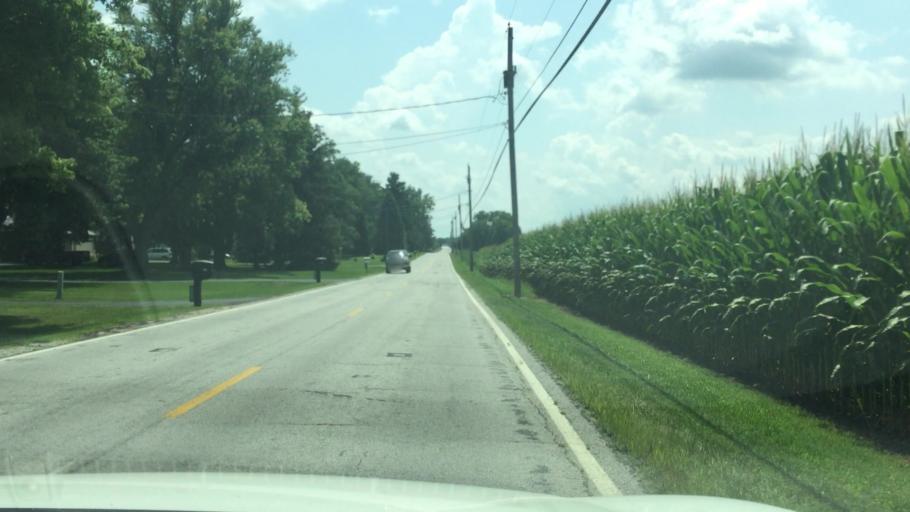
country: US
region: Ohio
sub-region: Clark County
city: Lisbon
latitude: 39.9348
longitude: -83.6822
